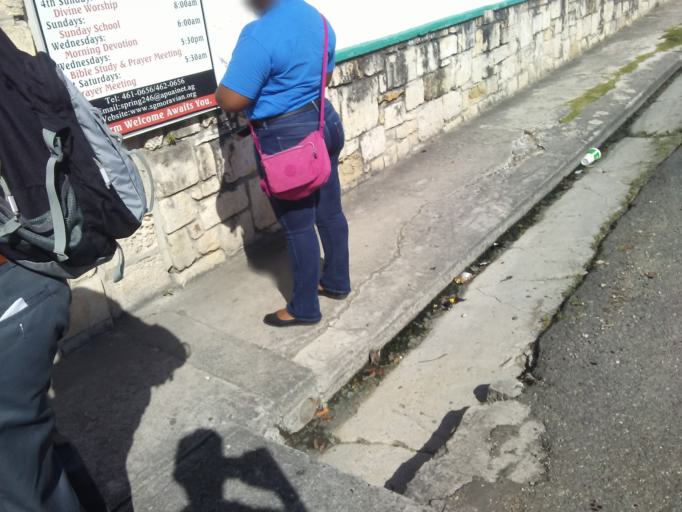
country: AG
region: Saint John
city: Saint John's
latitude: 17.1248
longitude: -61.8428
